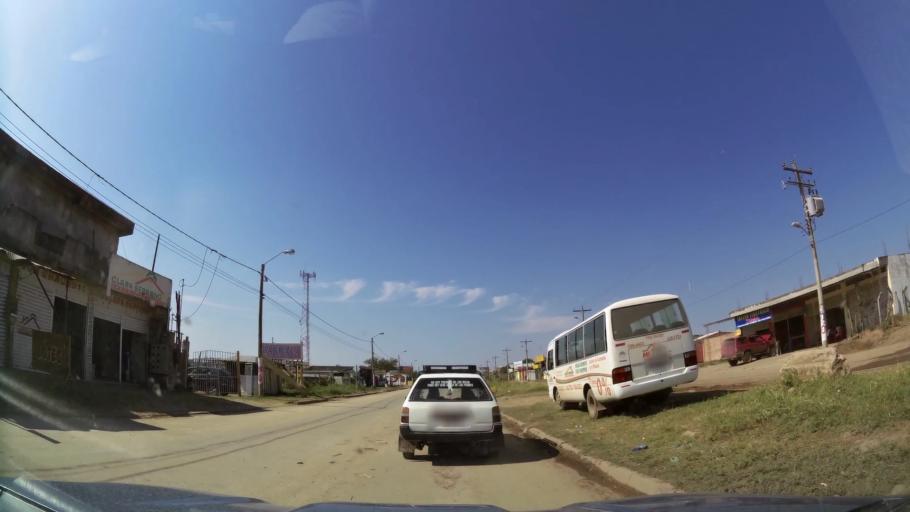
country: BO
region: Santa Cruz
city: Cotoca
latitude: -17.7335
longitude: -63.0987
